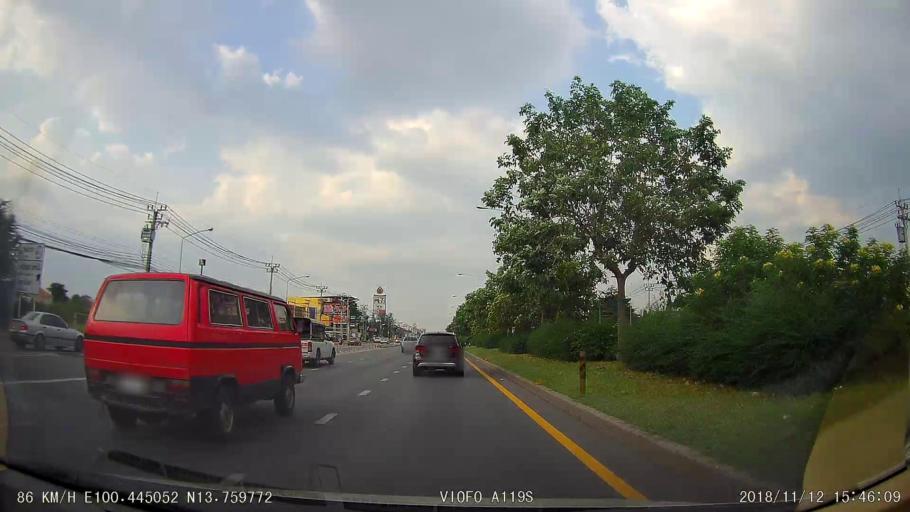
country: TH
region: Bangkok
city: Taling Chan
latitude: 13.7600
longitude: 100.4450
